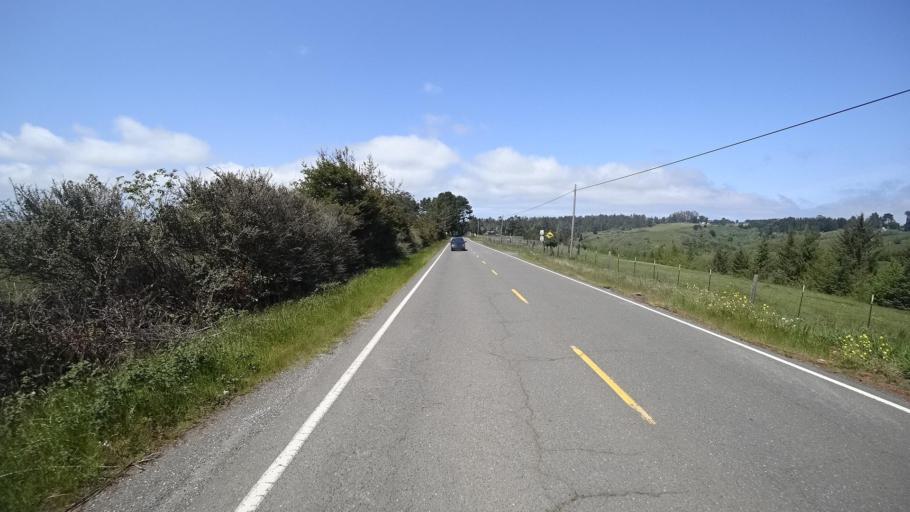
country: US
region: California
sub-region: Humboldt County
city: Fortuna
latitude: 40.6435
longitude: -124.2125
